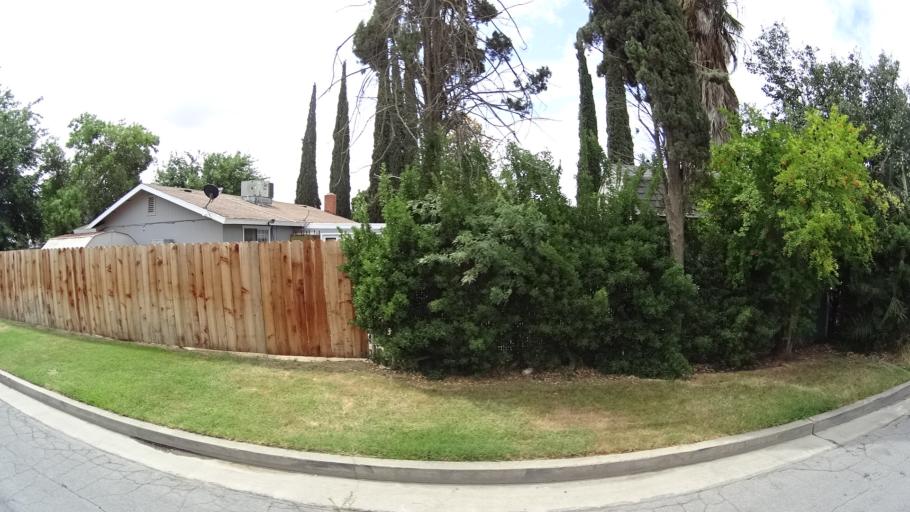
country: US
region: California
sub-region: Kings County
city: Home Garden
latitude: 36.3039
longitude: -119.6565
